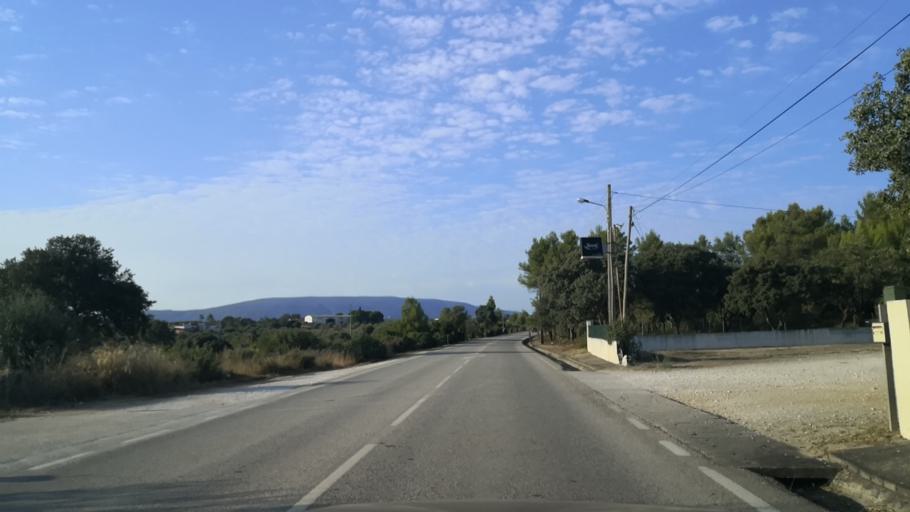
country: PT
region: Santarem
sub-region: Alcanena
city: Alcanena
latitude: 39.4253
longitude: -8.6345
